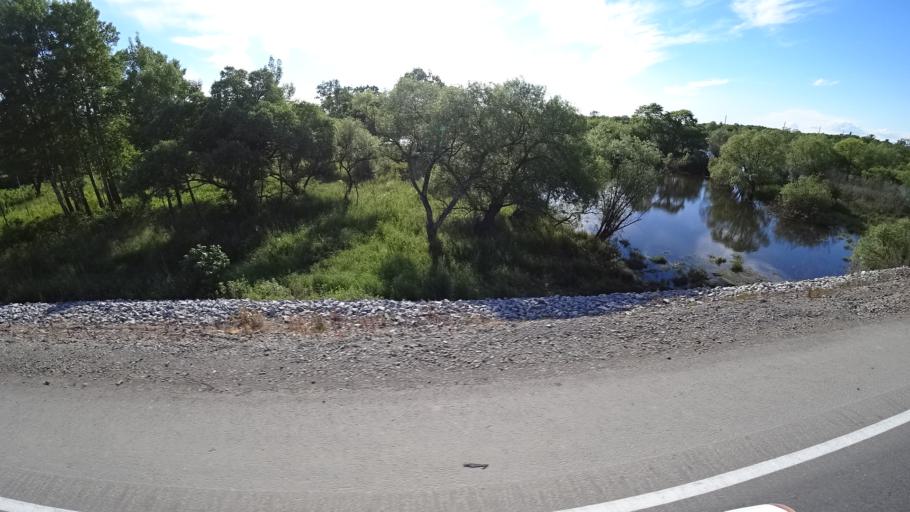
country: RU
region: Khabarovsk Krai
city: Khor
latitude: 47.8590
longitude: 134.9626
